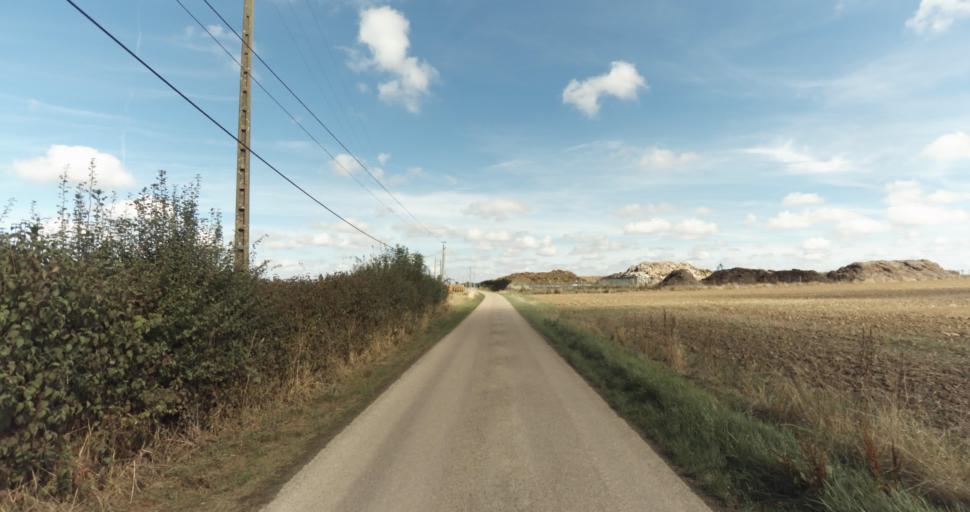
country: FR
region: Lower Normandy
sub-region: Departement du Calvados
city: Orbec
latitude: 48.9604
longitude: 0.4042
